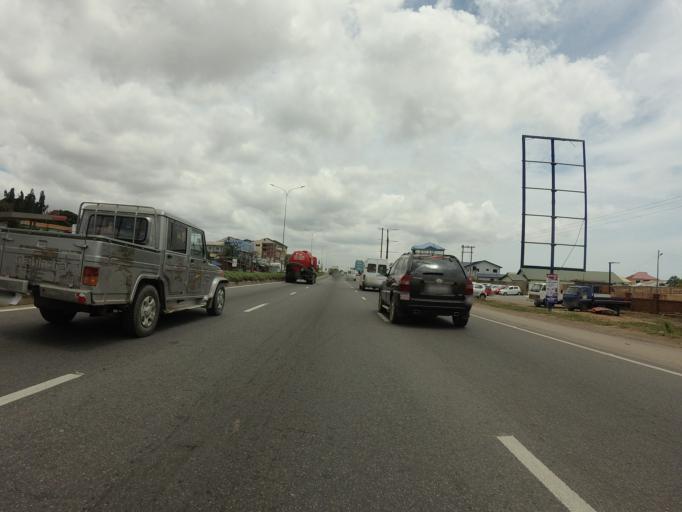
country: GH
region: Greater Accra
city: Gbawe
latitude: 5.5574
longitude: -0.2990
